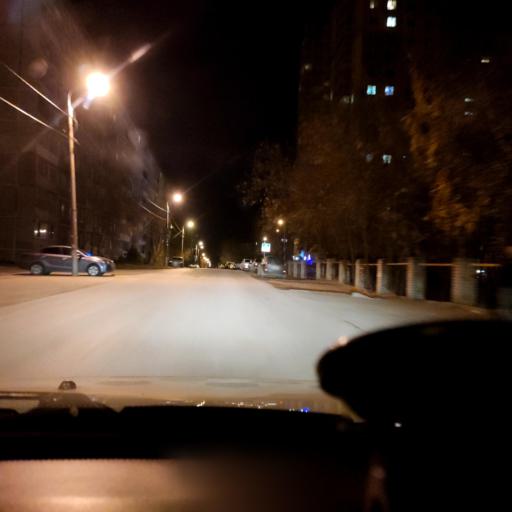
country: RU
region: Perm
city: Perm
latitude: 58.0998
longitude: 56.3003
